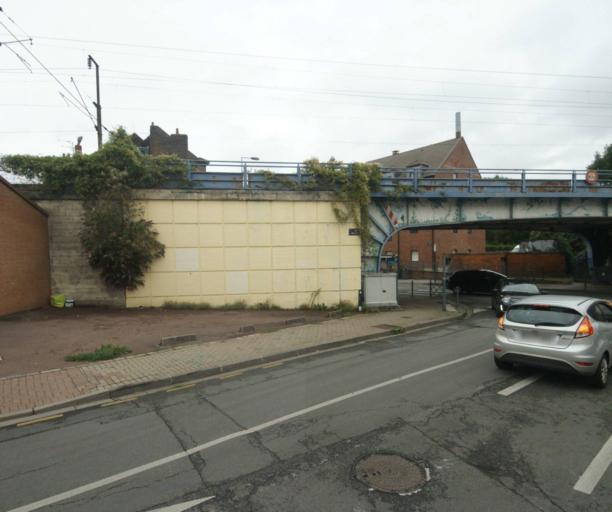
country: FR
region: Nord-Pas-de-Calais
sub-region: Departement du Nord
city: Ronchin
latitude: 50.6121
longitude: 3.0747
